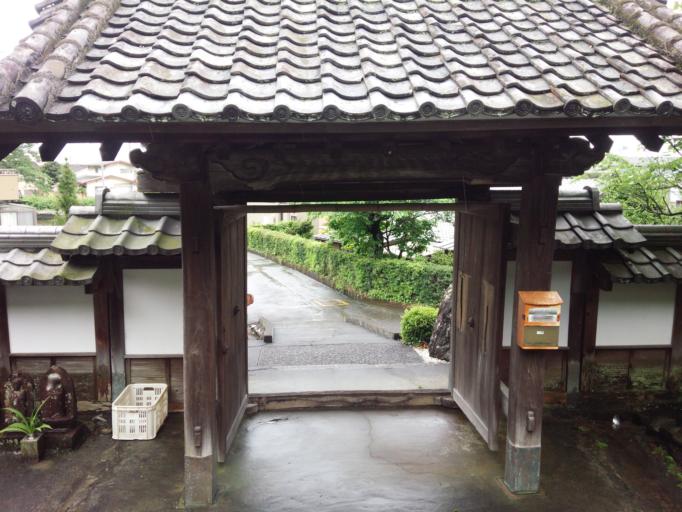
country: JP
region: Shizuoka
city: Shizuoka-shi
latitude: 35.0340
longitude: 138.4477
